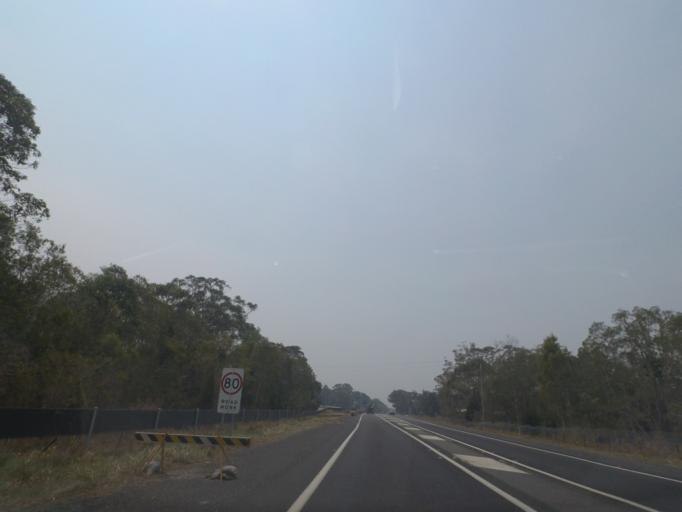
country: AU
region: New South Wales
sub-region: Ballina
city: Ballina
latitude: -28.9241
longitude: 153.4759
